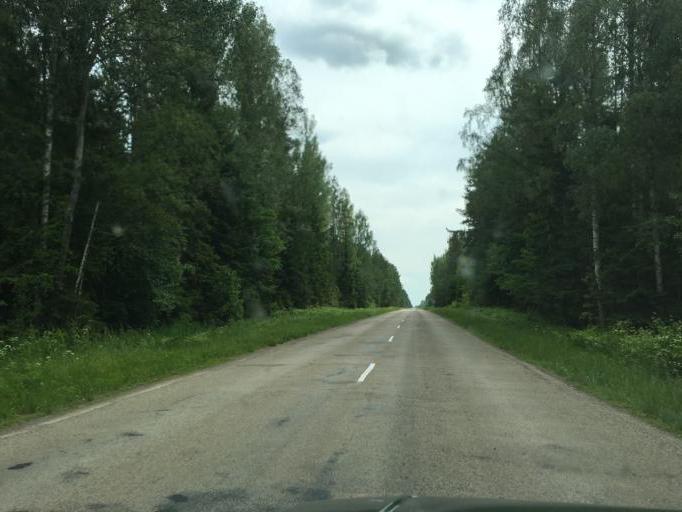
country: LV
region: Rugaju
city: Rugaji
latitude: 56.7796
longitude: 27.1045
